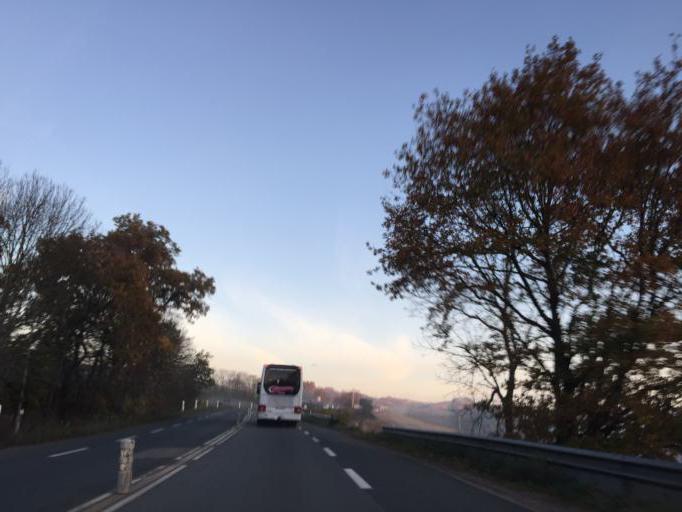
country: FR
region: Rhone-Alpes
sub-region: Departement de la Loire
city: Neulise
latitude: 45.8663
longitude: 4.1752
